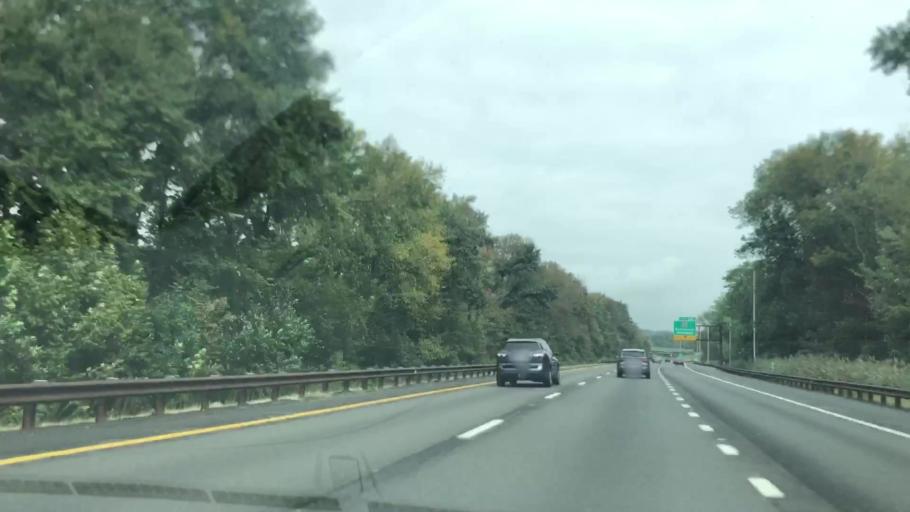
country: US
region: New Jersey
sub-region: Bergen County
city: Ho-Ho-Kus
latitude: 40.9931
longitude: -74.0726
